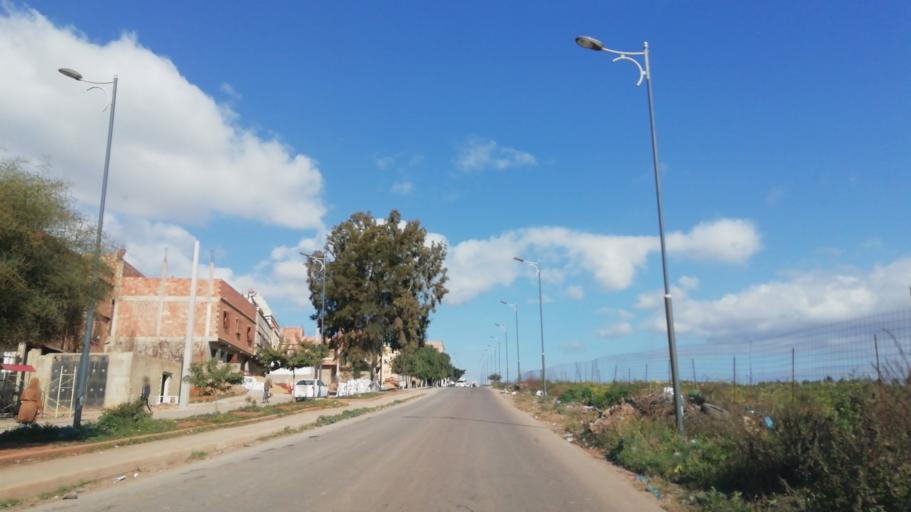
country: DZ
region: Oran
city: Es Senia
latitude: 35.6293
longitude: -0.6617
